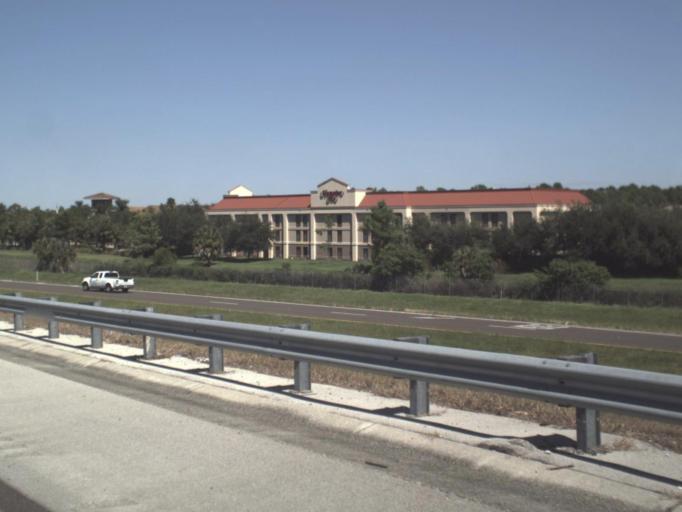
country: US
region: Florida
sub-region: Collier County
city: Vineyards
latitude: 26.2745
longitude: -81.7425
